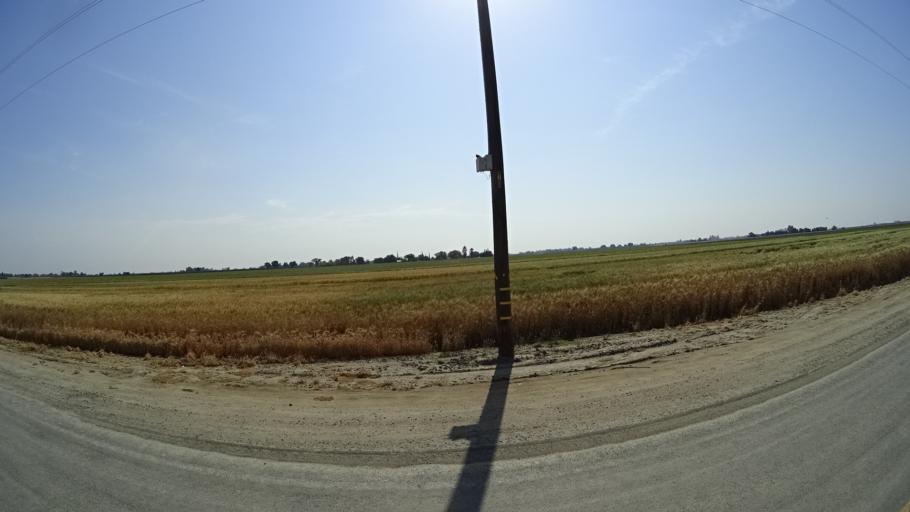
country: US
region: California
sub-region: Kings County
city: Lemoore
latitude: 36.3215
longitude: -119.8438
